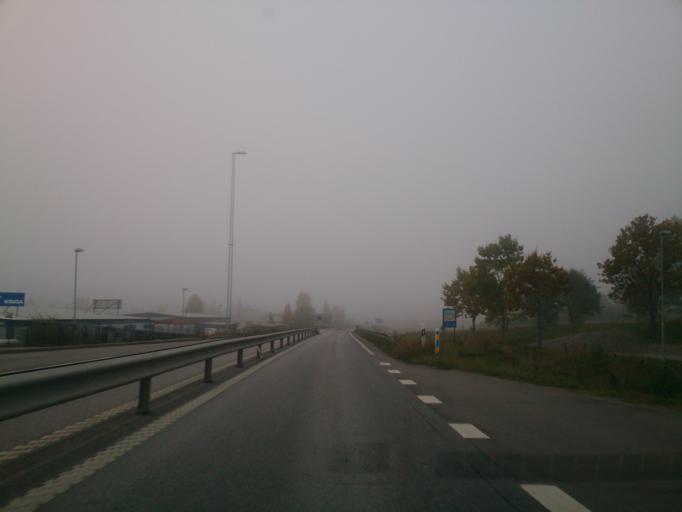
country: SE
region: OEstergoetland
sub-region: Kinda Kommun
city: Rimforsa
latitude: 58.1380
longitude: 15.6802
